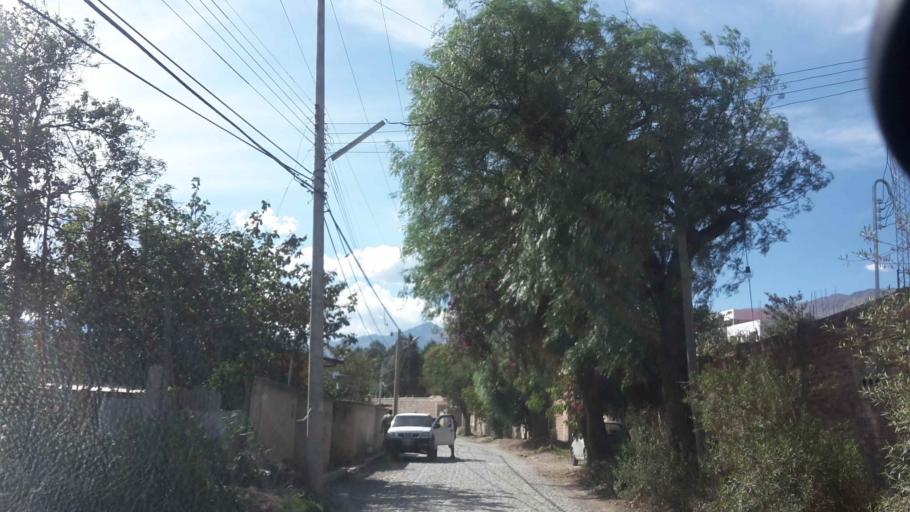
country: BO
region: Cochabamba
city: Cochabamba
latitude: -17.3538
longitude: -66.1983
